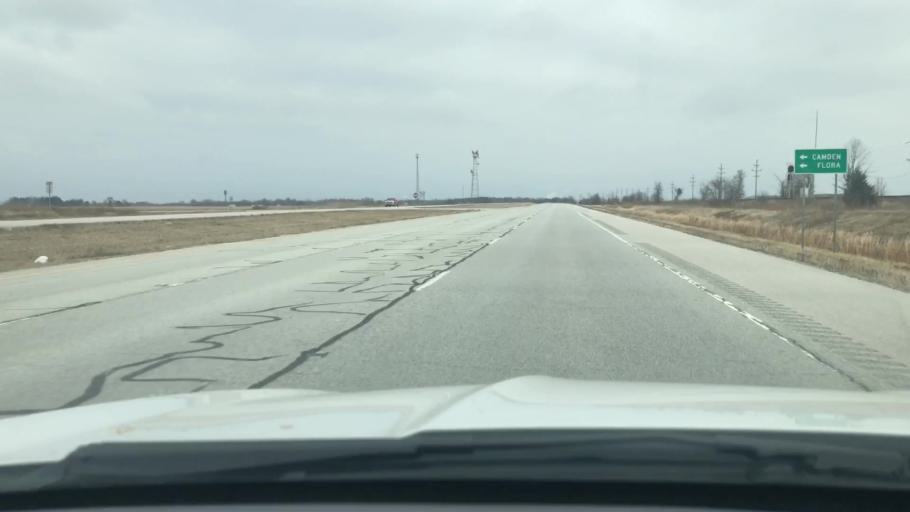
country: US
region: Indiana
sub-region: Cass County
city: Georgetown
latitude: 40.6627
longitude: -86.5350
